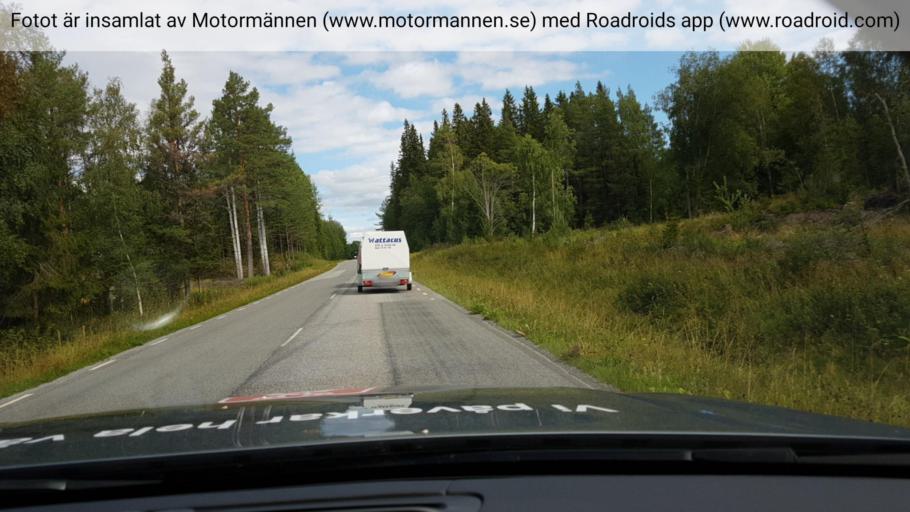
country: SE
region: Jaemtland
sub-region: Krokoms Kommun
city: Krokom
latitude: 63.3303
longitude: 14.2009
